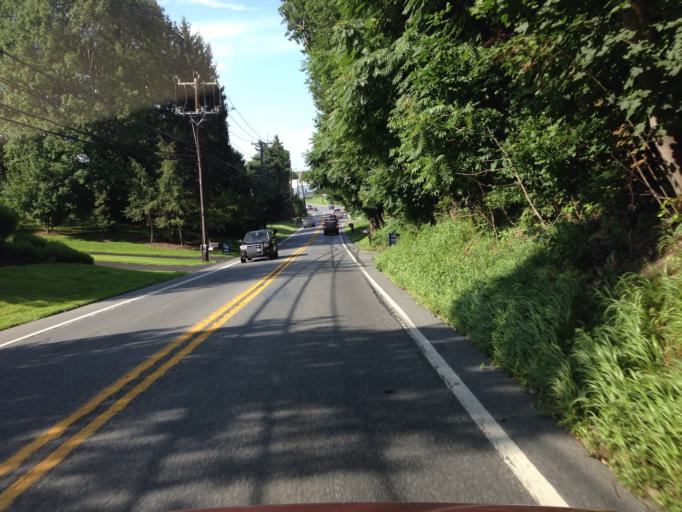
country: US
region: Pennsylvania
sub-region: Lancaster County
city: East Petersburg
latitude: 40.0927
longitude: -76.3297
